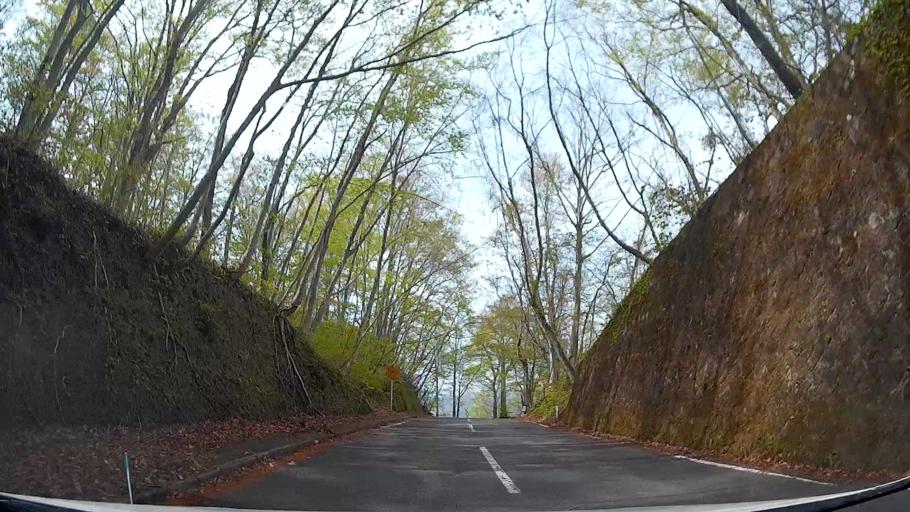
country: JP
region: Akita
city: Hanawa
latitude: 40.4352
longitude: 140.9156
